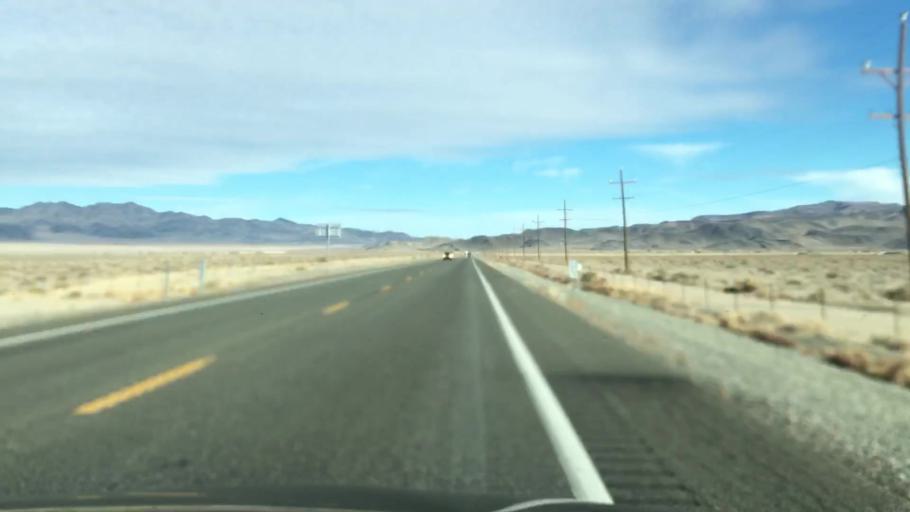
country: US
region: Nevada
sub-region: Mineral County
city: Hawthorne
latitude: 38.5254
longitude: -118.5731
